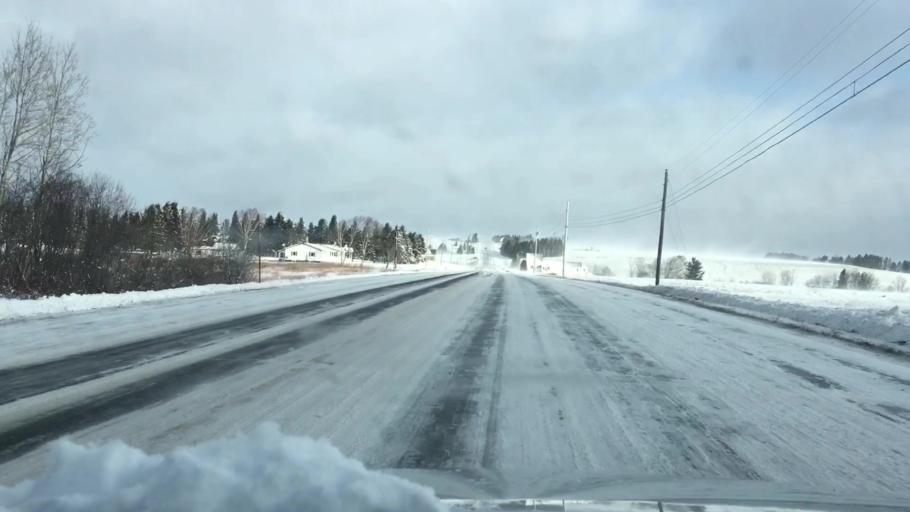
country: US
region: Maine
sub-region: Aroostook County
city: Van Buren
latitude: 47.0994
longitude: -67.9752
